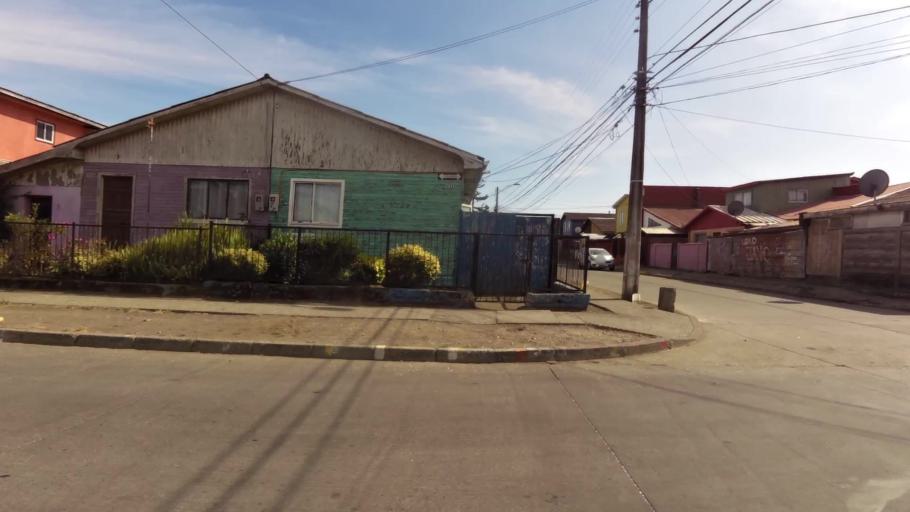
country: CL
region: Biobio
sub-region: Provincia de Concepcion
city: Talcahuano
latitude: -36.7846
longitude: -73.1047
